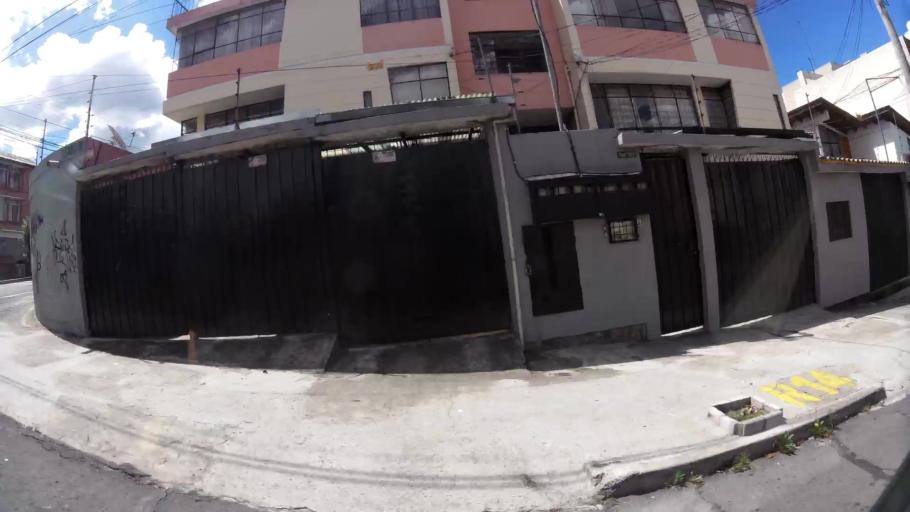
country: EC
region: Pichincha
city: Quito
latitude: -0.1906
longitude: -78.5018
